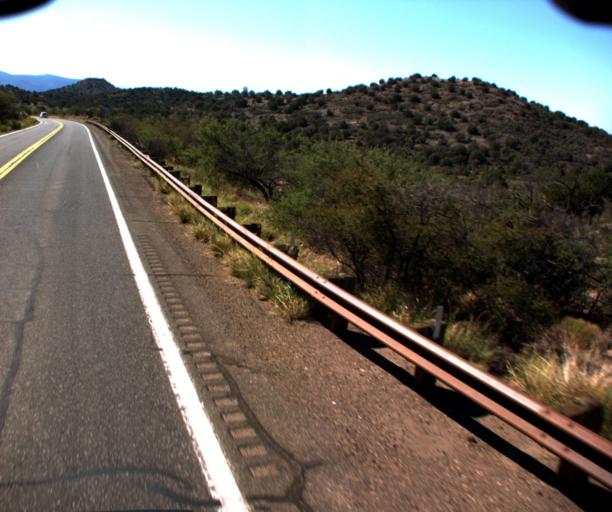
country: US
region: Arizona
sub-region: Yavapai County
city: Lake Montezuma
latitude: 34.6936
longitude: -111.7525
